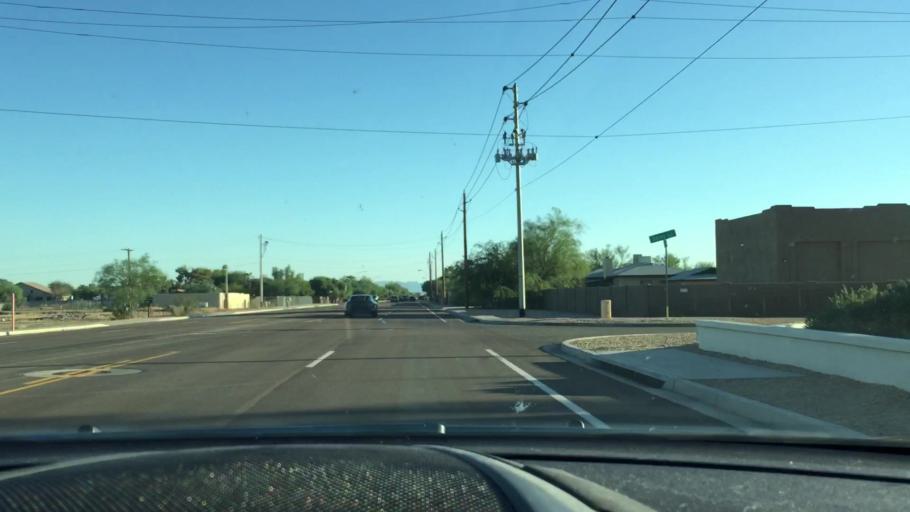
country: US
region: Arizona
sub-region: Maricopa County
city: Sun City
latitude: 33.6909
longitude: -112.2377
